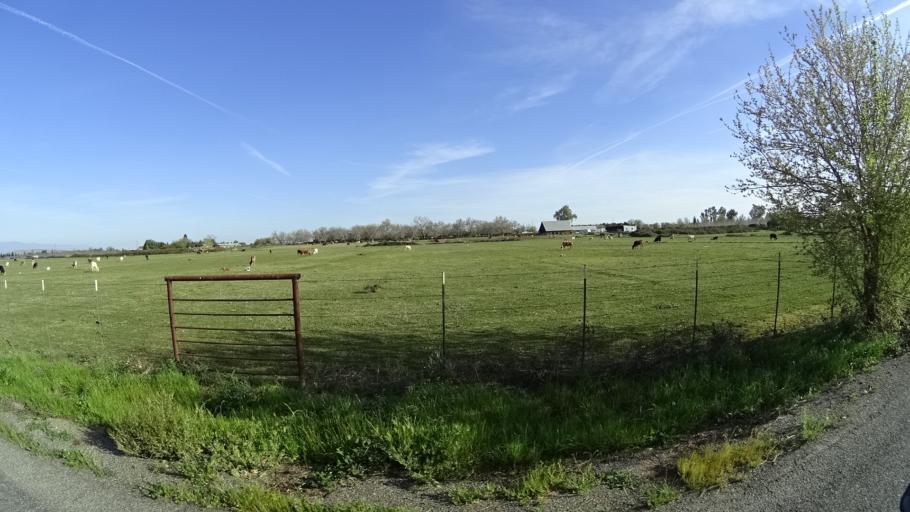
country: US
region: California
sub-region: Glenn County
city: Orland
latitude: 39.7151
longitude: -122.2315
